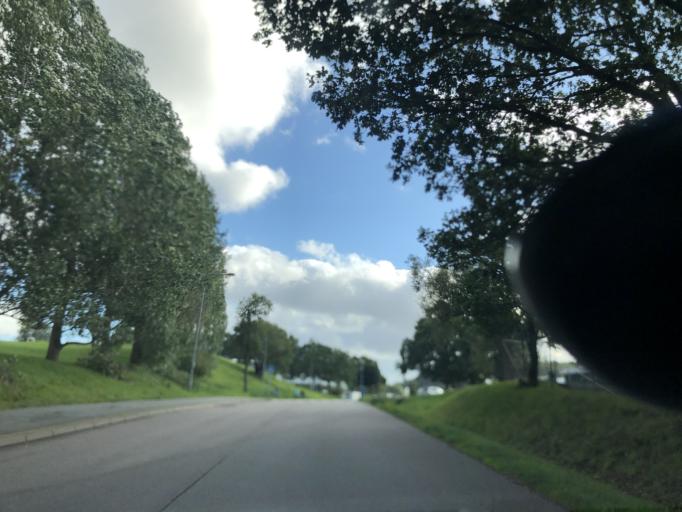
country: SE
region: Vaestra Goetaland
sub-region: Goteborg
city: Goeteborg
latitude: 57.7478
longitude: 11.9432
